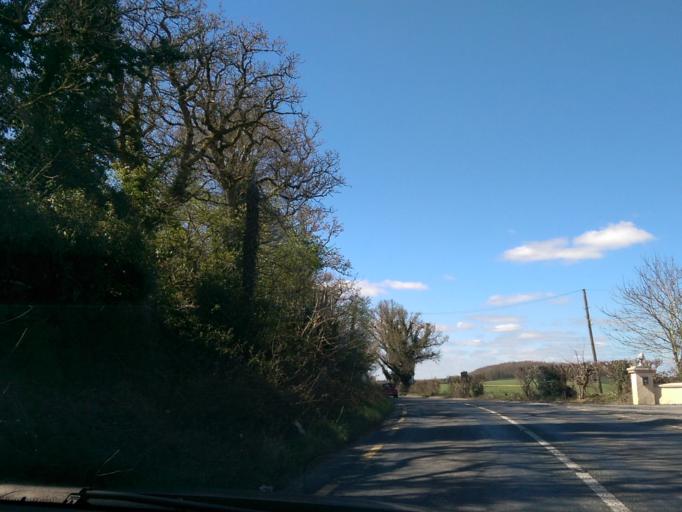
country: IE
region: Leinster
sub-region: Laois
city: Stradbally
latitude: 53.0149
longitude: -7.0866
